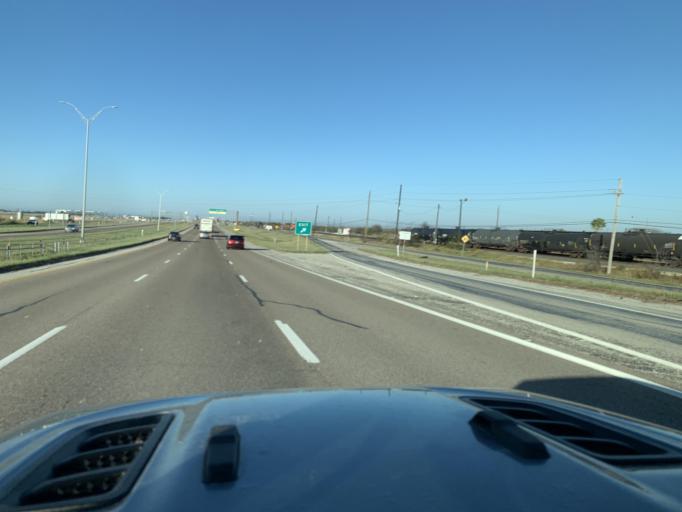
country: US
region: Texas
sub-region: Nueces County
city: Corpus Christi
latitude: 27.7851
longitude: -97.4897
